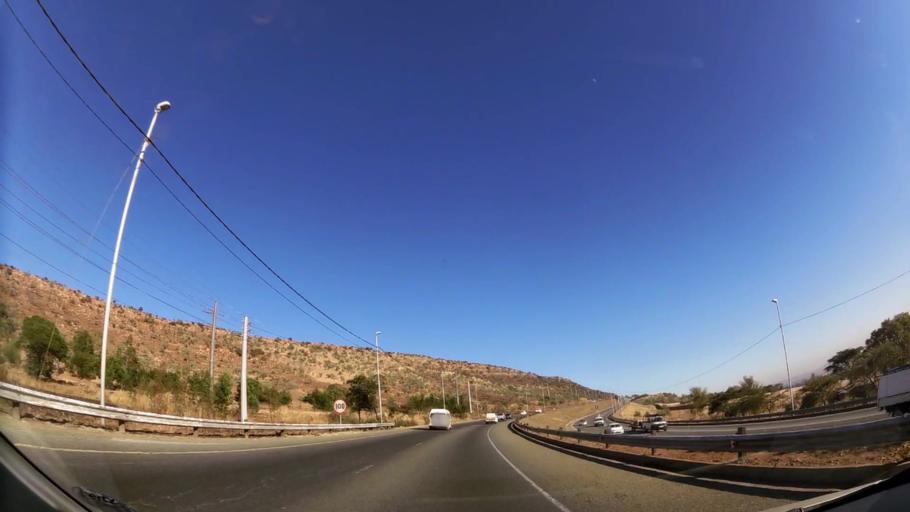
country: ZA
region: Gauteng
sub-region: West Rand District Municipality
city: Muldersdriseloop
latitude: -26.0676
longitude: 27.8216
